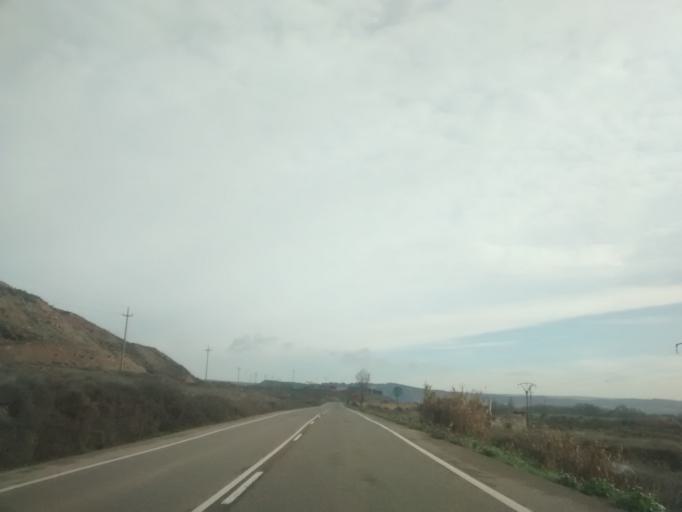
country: ES
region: La Rioja
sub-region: Provincia de La Rioja
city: Alcanadre
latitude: 42.4182
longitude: -2.1139
